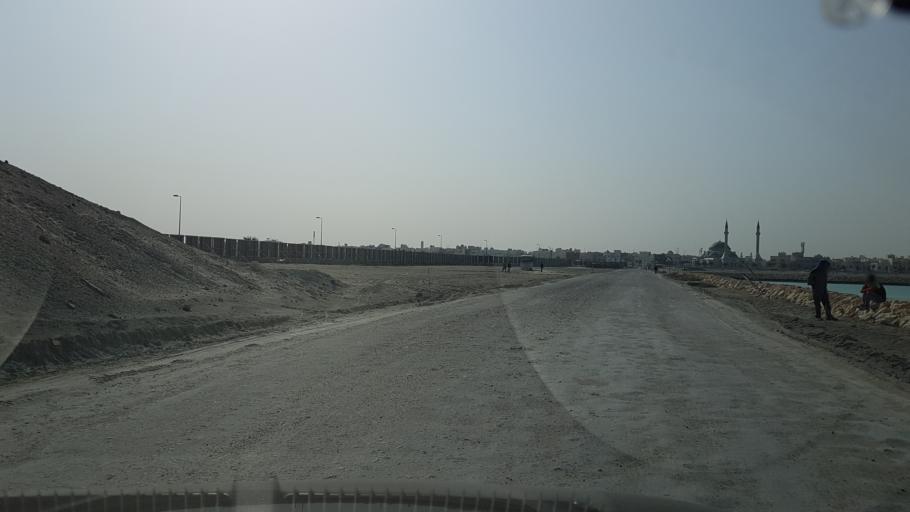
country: BH
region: Muharraq
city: Al Hadd
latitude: 26.2714
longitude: 50.6672
